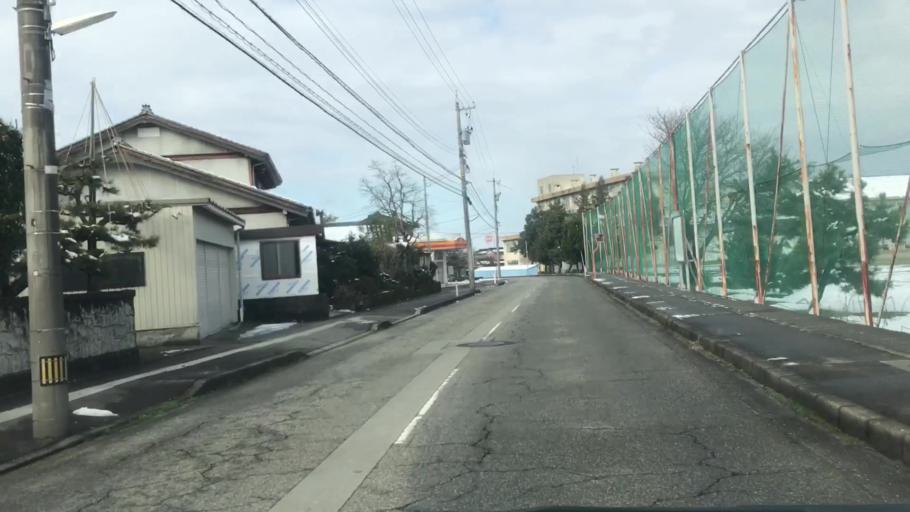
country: JP
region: Toyama
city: Toyama-shi
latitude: 36.6160
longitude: 137.2535
